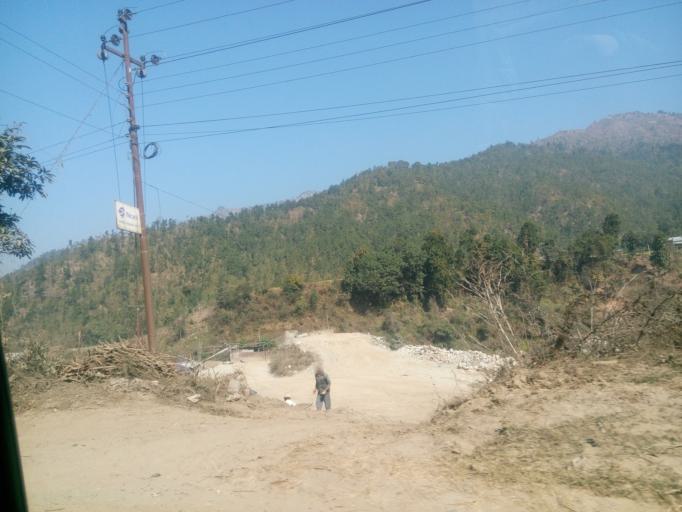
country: NP
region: Central Region
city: Kirtipur
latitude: 27.7671
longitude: 85.0395
